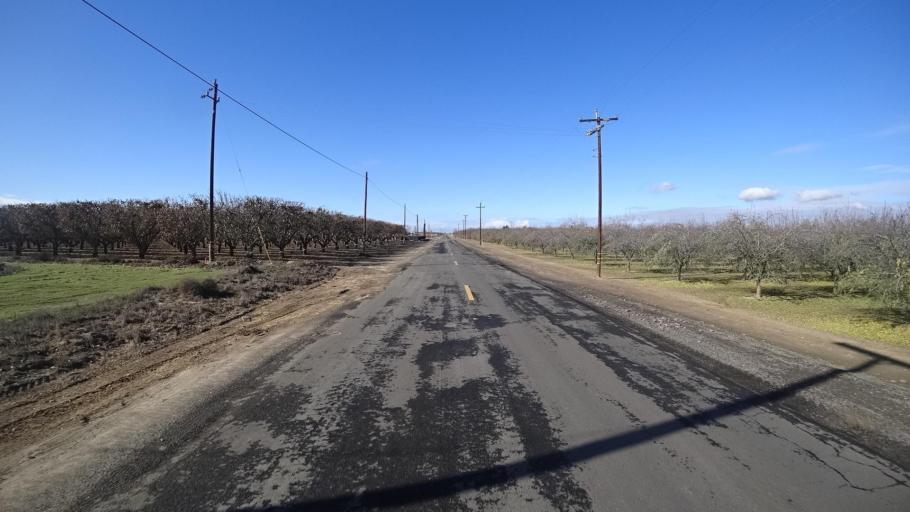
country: US
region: California
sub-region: Kern County
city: Rosedale
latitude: 35.3689
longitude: -119.2102
